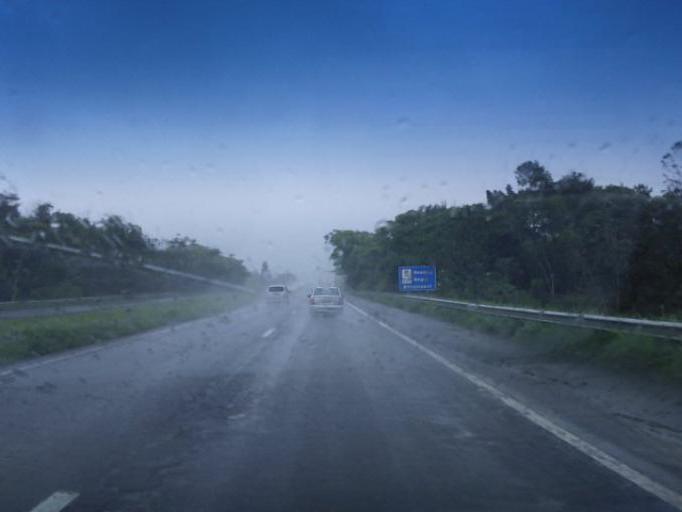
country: BR
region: Sao Paulo
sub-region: Pariquera-Acu
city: Pariquera Acu
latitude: -24.6399
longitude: -47.9137
